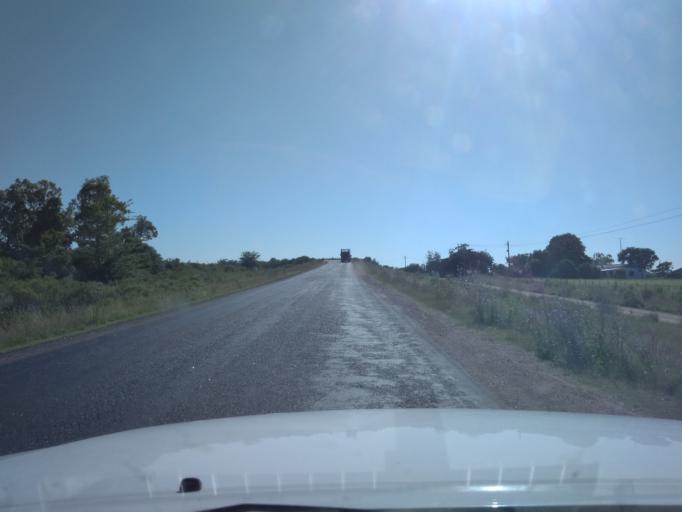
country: UY
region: Canelones
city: San Ramon
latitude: -34.2675
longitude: -55.9326
